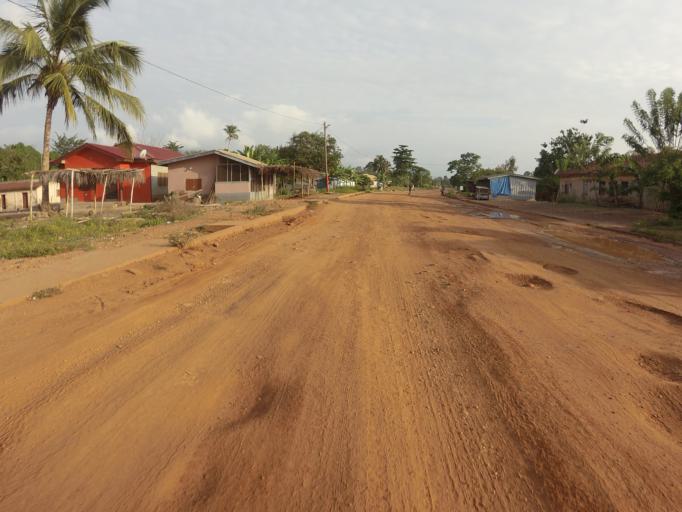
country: GH
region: Volta
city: Kpandu
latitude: 6.9613
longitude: 0.4598
